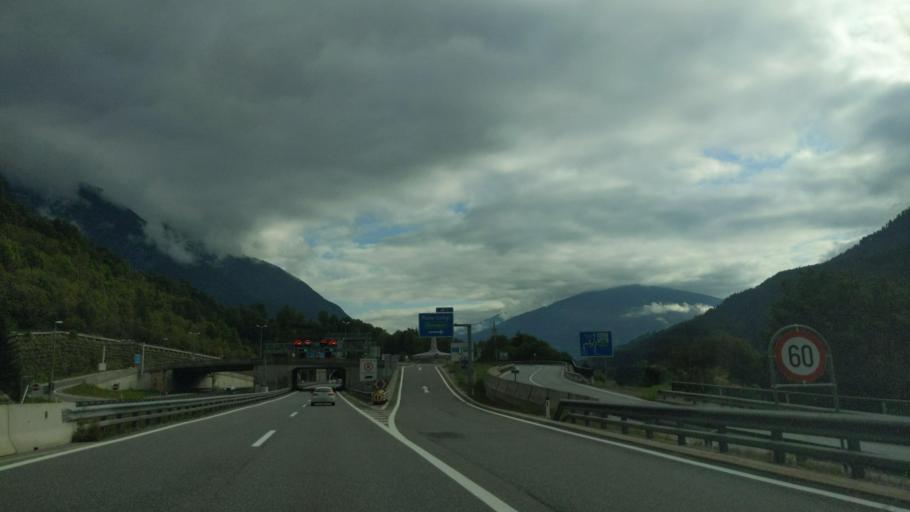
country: AT
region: Tyrol
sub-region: Politischer Bezirk Landeck
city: Pians
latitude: 47.1293
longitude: 10.4990
